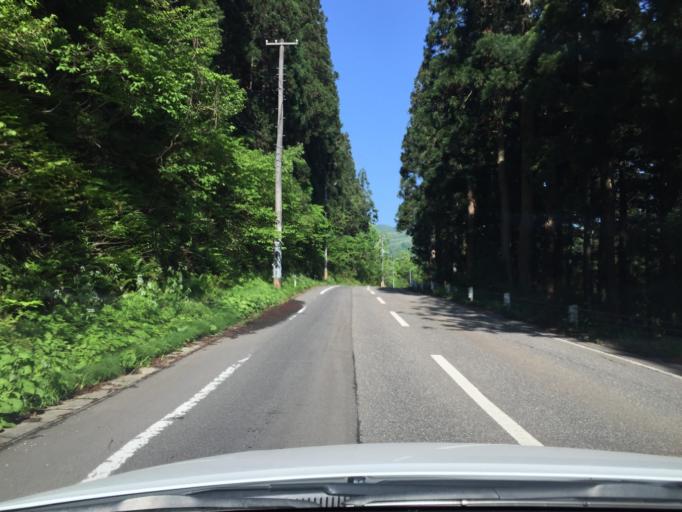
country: JP
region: Fukushima
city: Kitakata
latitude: 37.6702
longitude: 139.5869
